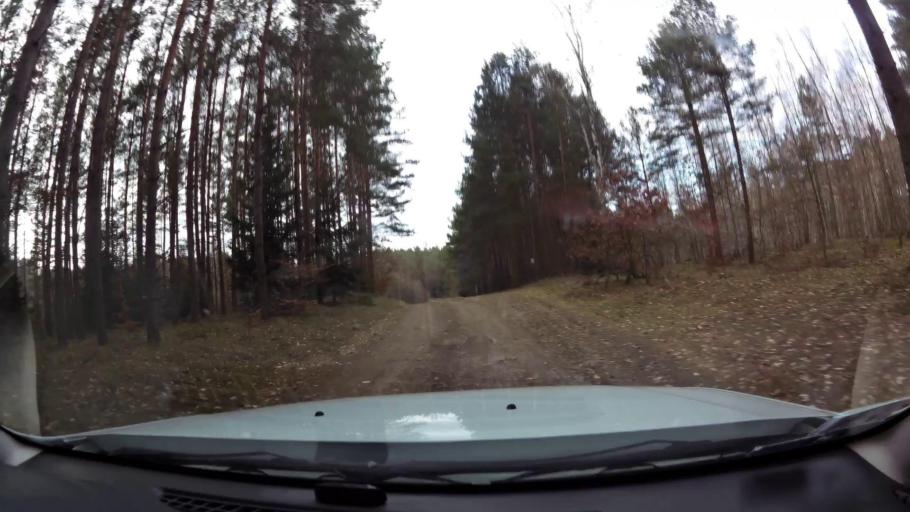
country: PL
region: West Pomeranian Voivodeship
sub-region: Powiat drawski
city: Drawsko Pomorskie
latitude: 53.5354
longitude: 15.6969
